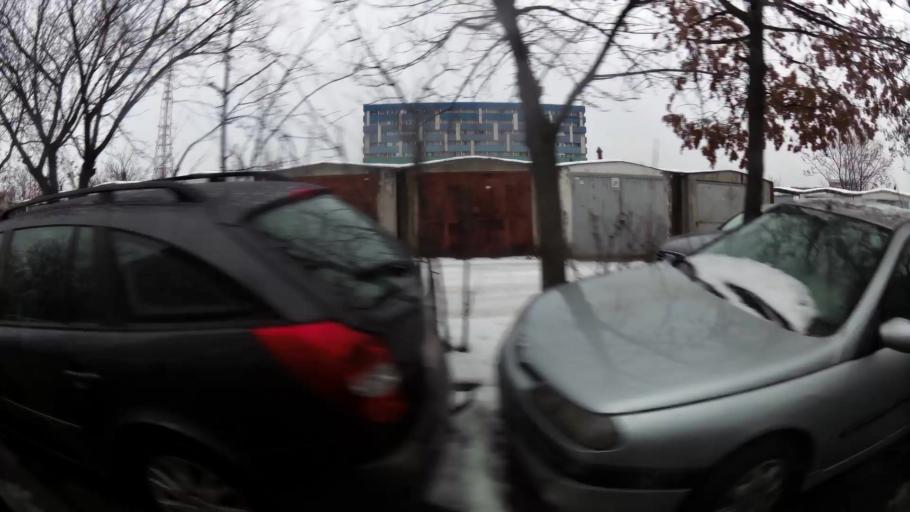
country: RO
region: Ilfov
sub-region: Comuna Chiajna
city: Rosu
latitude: 44.4385
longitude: 26.0394
